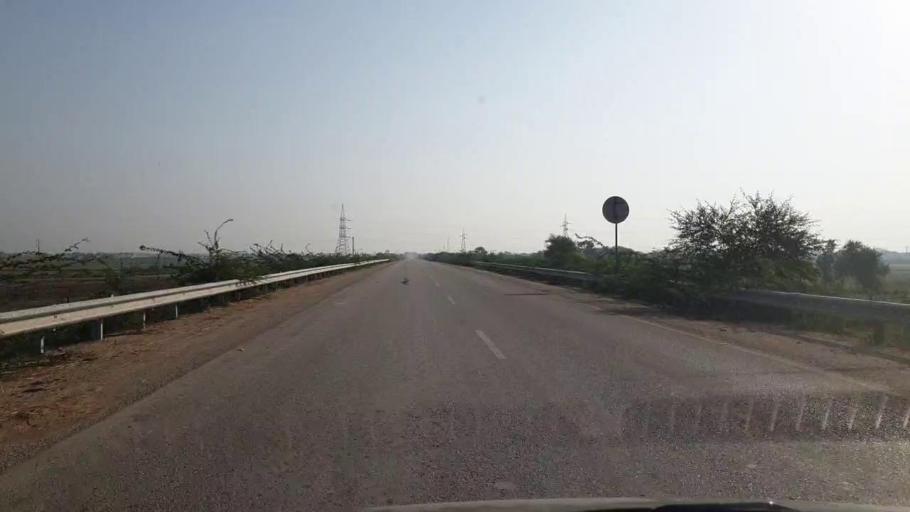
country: PK
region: Sindh
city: Badin
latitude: 24.6786
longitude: 68.8182
